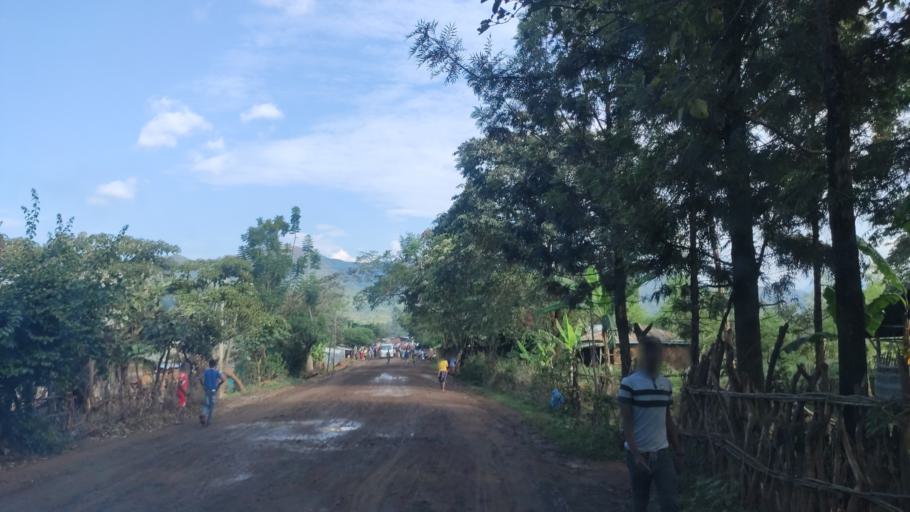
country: ET
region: Southern Nations, Nationalities, and People's Region
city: Felege Neway
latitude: 6.4257
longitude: 37.3077
